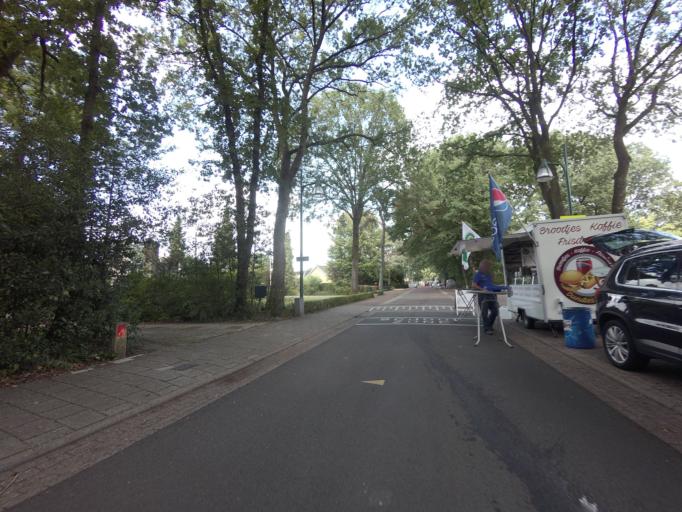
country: NL
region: Overijssel
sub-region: Gemeente Staphorst
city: Staphorst
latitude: 52.6580
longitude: 6.2912
